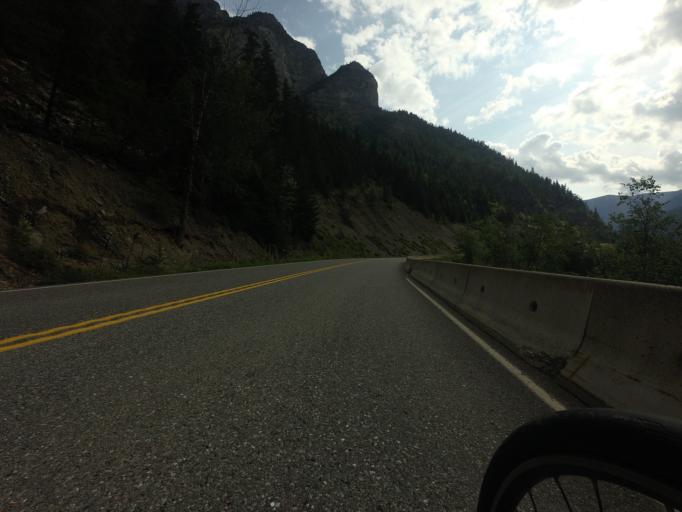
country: CA
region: British Columbia
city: Lillooet
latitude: 50.6418
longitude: -122.0503
